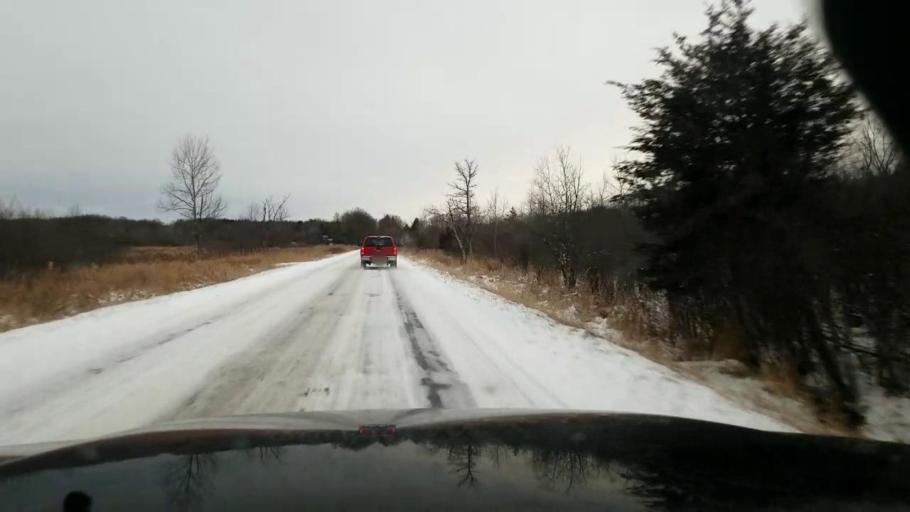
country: US
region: Michigan
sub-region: Jackson County
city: Spring Arbor
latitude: 42.1263
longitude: -84.4983
